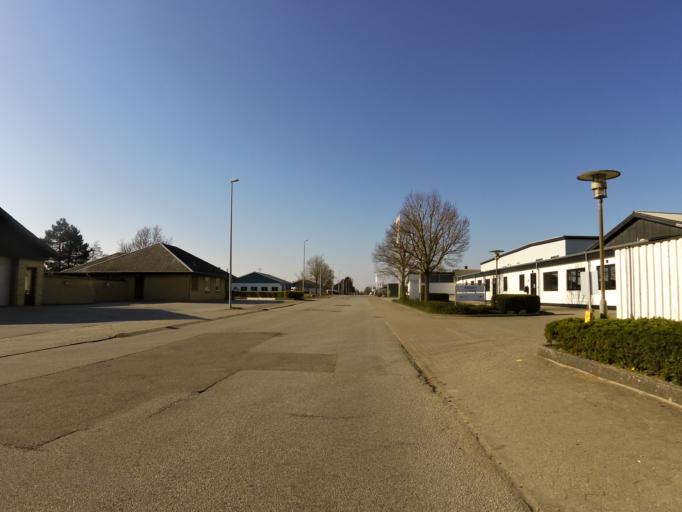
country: DK
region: South Denmark
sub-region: Esbjerg Kommune
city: Ribe
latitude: 55.3491
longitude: 8.7742
